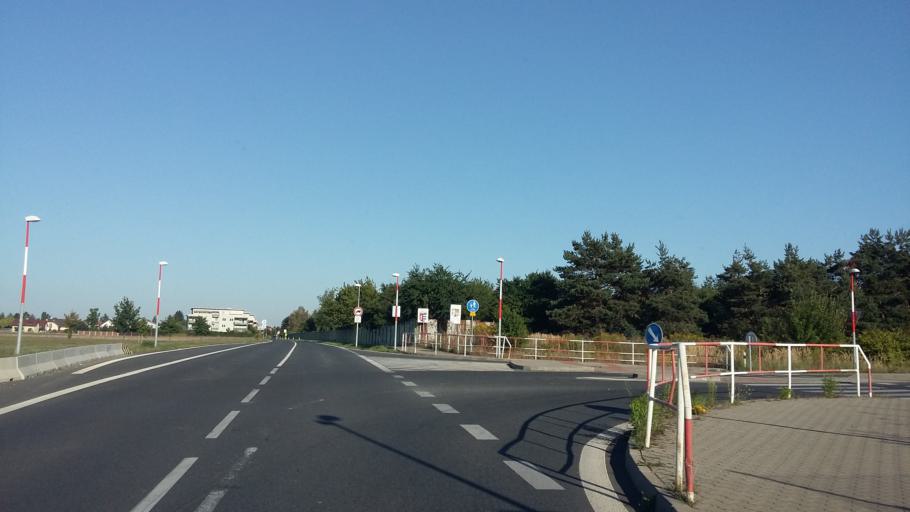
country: CZ
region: Praha
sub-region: Praha 19
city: Kbely
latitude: 50.1353
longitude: 14.5345
